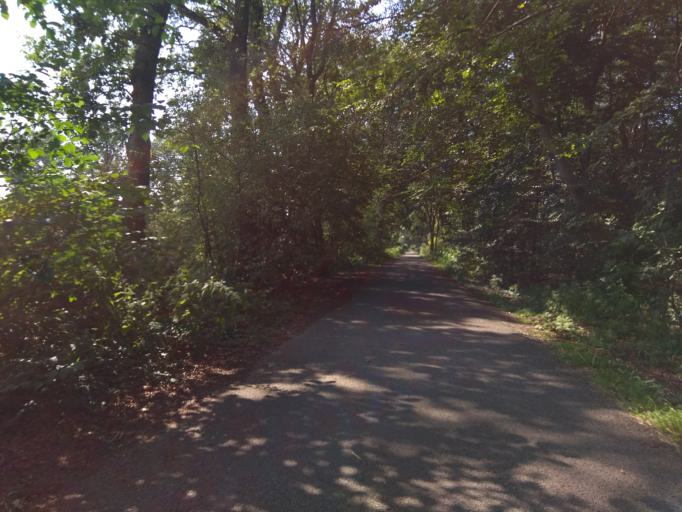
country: DE
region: North Rhine-Westphalia
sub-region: Regierungsbezirk Munster
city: Klein Reken
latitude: 51.7286
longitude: 7.0212
